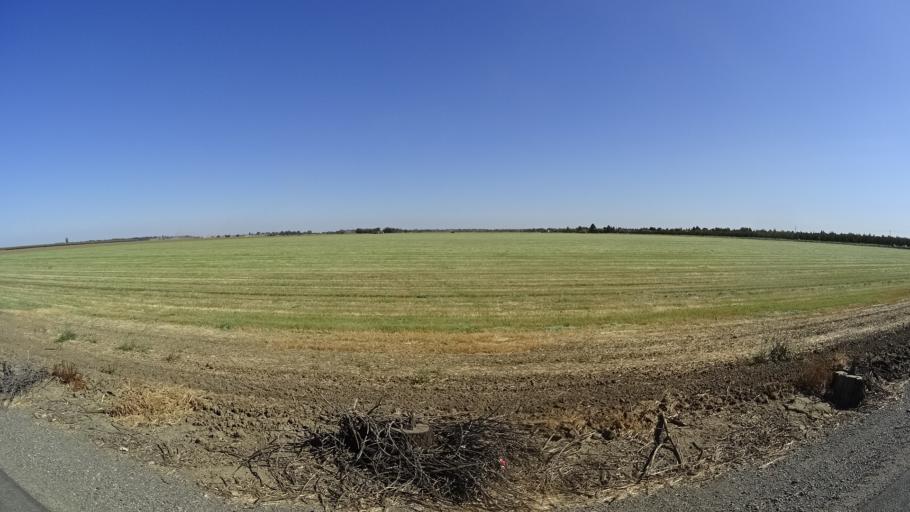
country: US
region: California
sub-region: Yolo County
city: Davis
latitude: 38.5636
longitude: -121.8032
